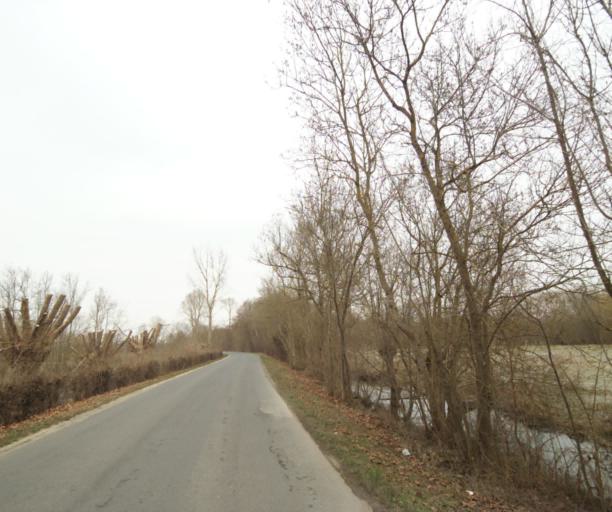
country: FR
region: Poitou-Charentes
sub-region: Departement des Deux-Sevres
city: Bessines
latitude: 46.3048
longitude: -0.5166
